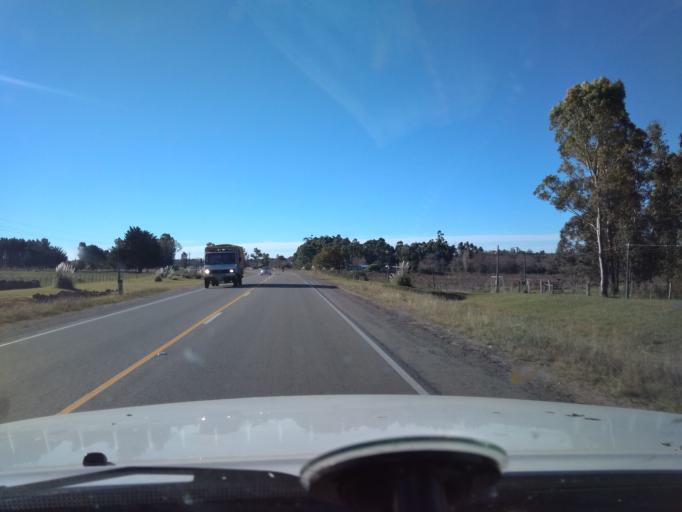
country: UY
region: Canelones
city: Sauce
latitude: -34.6104
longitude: -56.0485
